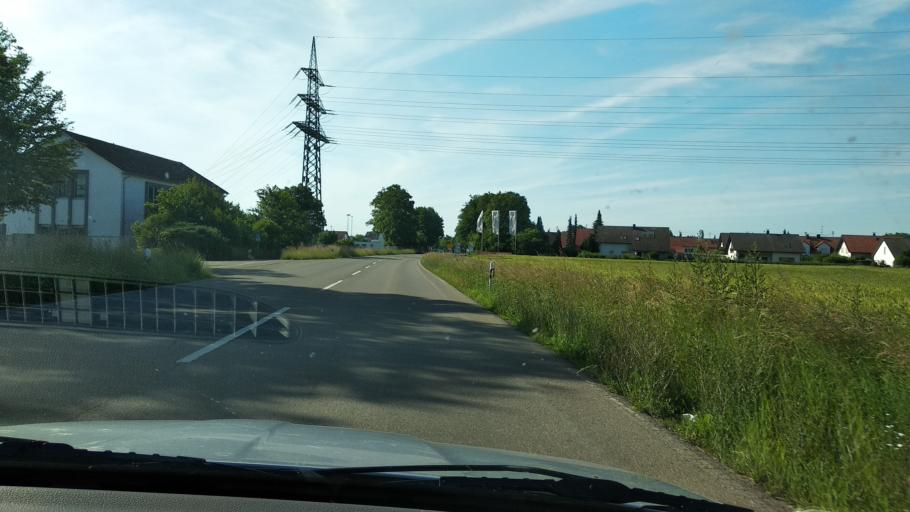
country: DE
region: Bavaria
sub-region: Swabia
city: Vohringen
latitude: 48.2688
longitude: 10.0852
